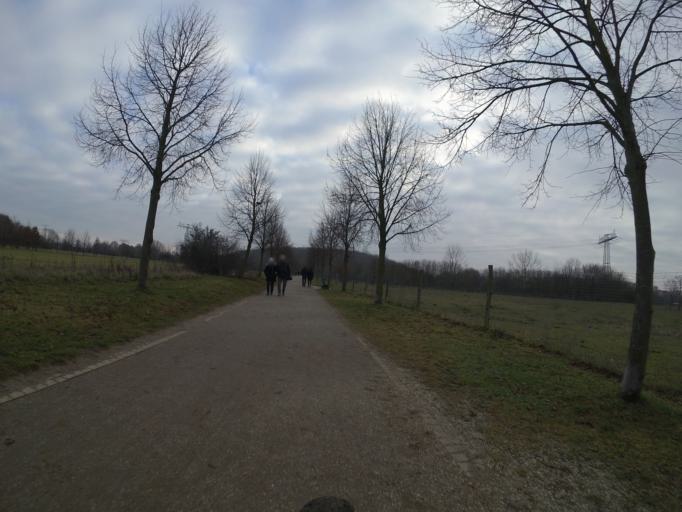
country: DE
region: Brandenburg
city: Ahrensfelde
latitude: 52.5625
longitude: 13.5812
